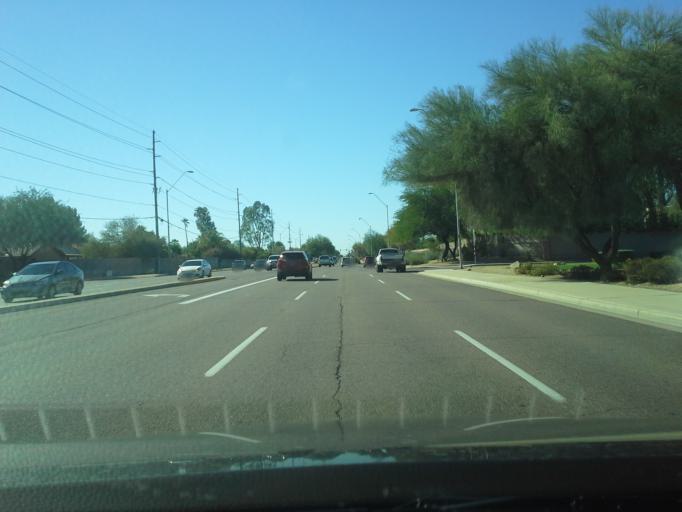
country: US
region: Arizona
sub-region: Maricopa County
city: Paradise Valley
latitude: 33.6406
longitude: -111.9640
